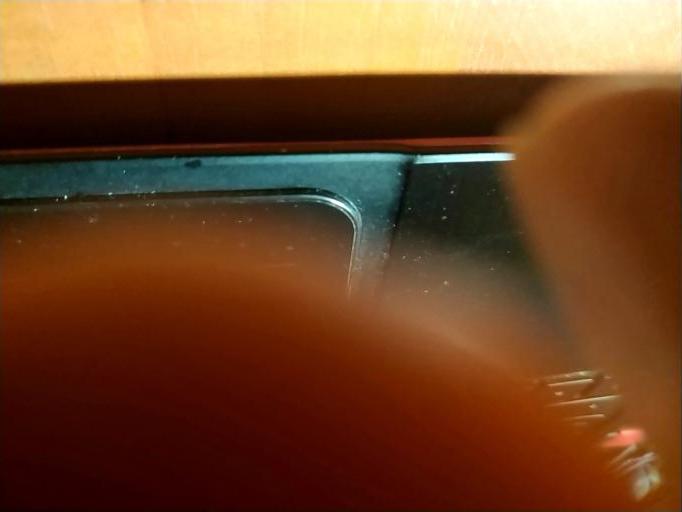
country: RU
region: Tverskaya
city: Ves'yegonsk
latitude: 58.7039
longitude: 37.5439
